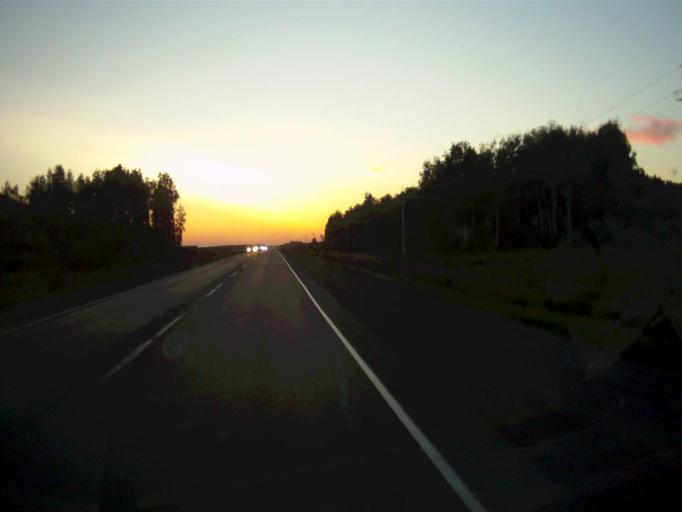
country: RU
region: Chelyabinsk
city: Poletayevo
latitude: 55.2130
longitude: 61.0671
